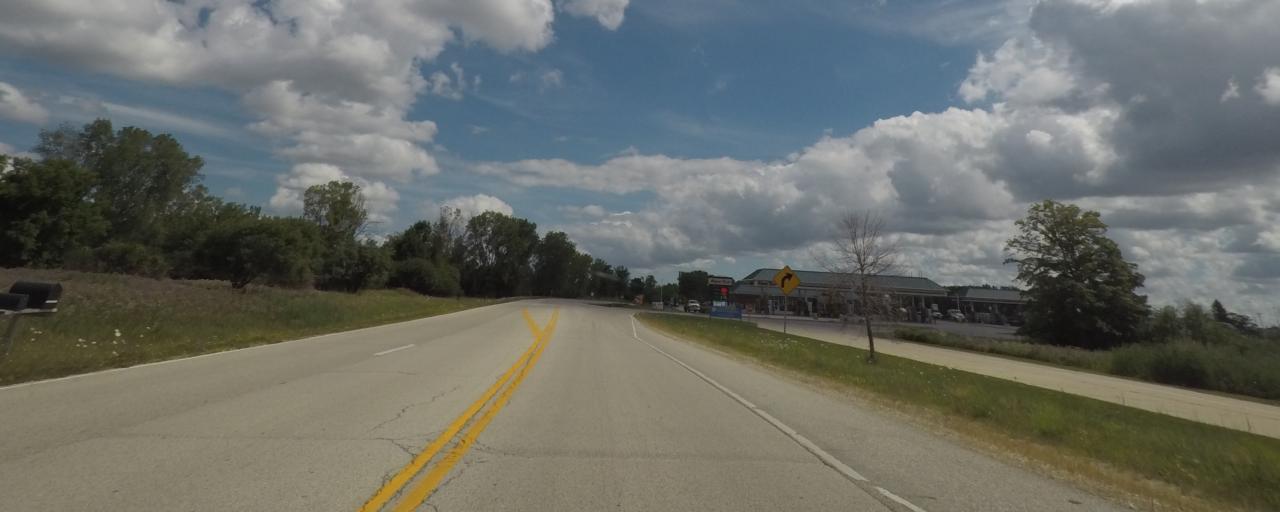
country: US
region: Wisconsin
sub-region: Waukesha County
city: Pewaukee
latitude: 43.0477
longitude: -88.2601
